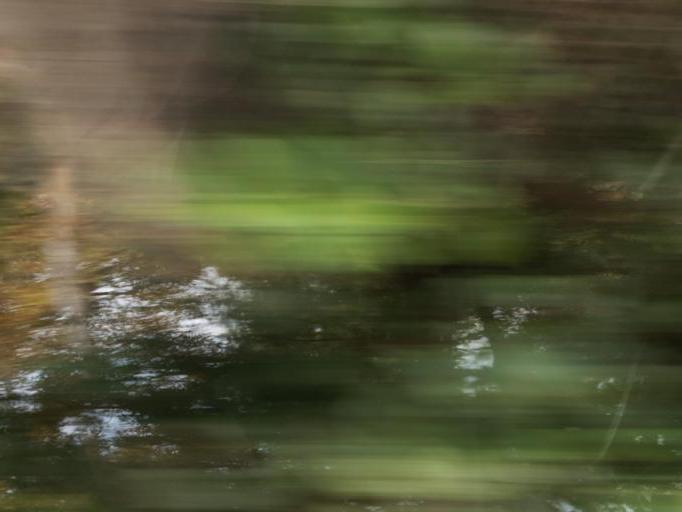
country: TR
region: Kirikkale
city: Bahsili
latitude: 39.8088
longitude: 33.4703
